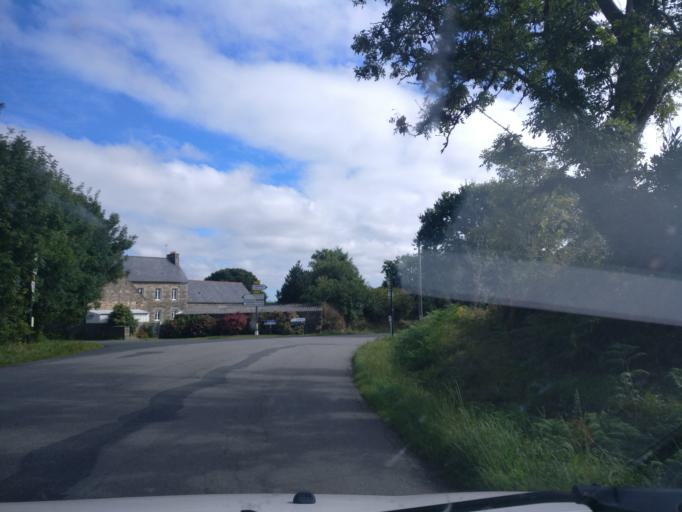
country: FR
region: Brittany
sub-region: Departement des Cotes-d'Armor
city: Rospez
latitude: 48.7356
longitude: -3.3750
